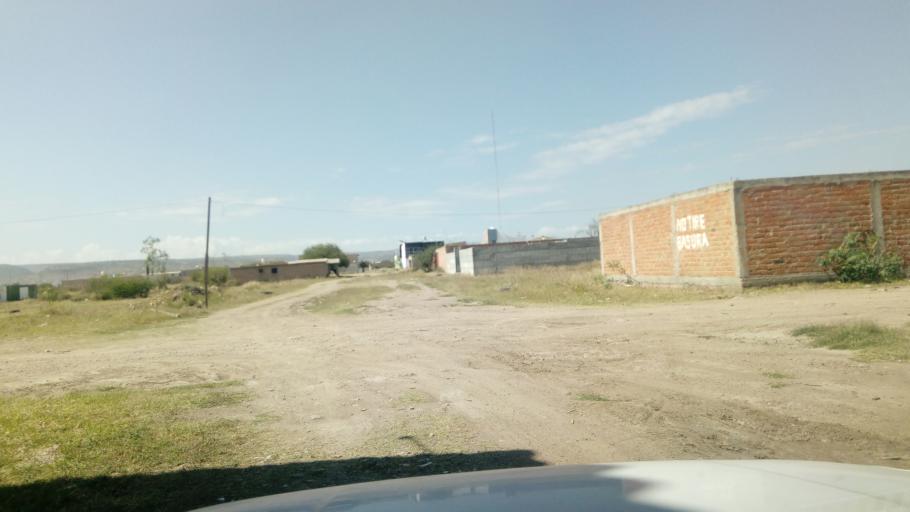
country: MX
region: Durango
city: Victoria de Durango
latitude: 23.9876
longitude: -104.6821
